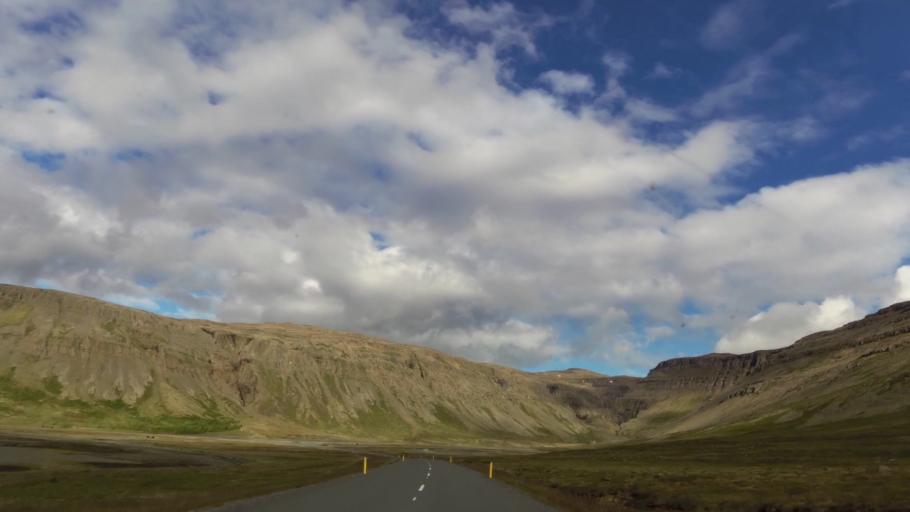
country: IS
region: West
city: Olafsvik
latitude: 65.5138
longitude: -23.8465
